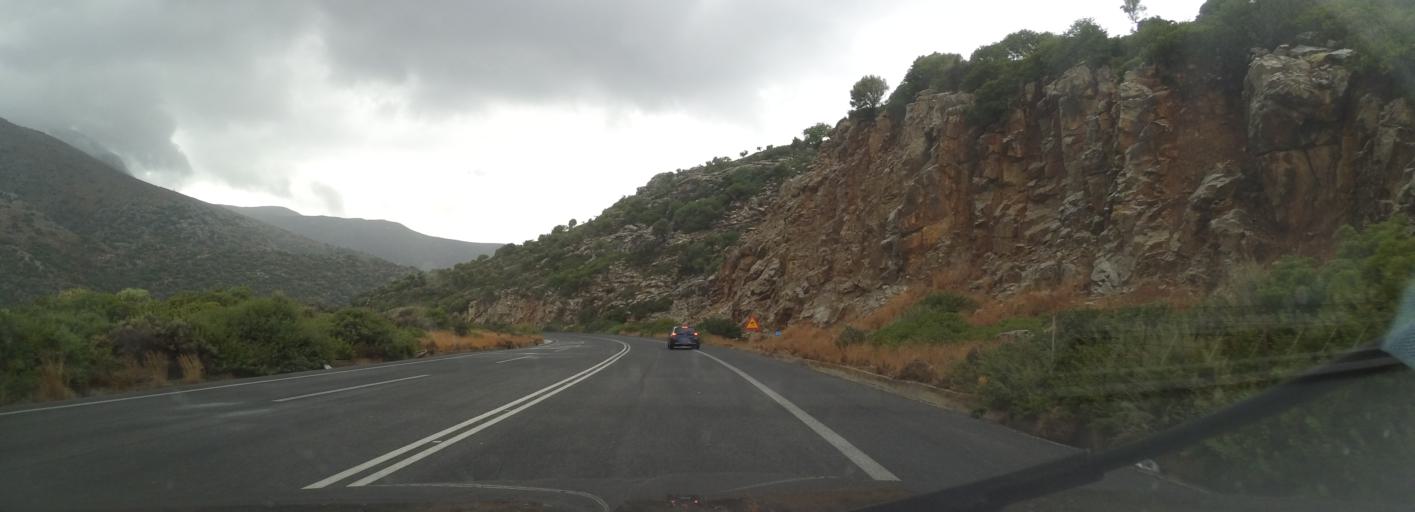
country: GR
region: Crete
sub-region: Nomos Irakleiou
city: Tilisos
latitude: 35.4039
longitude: 24.9826
